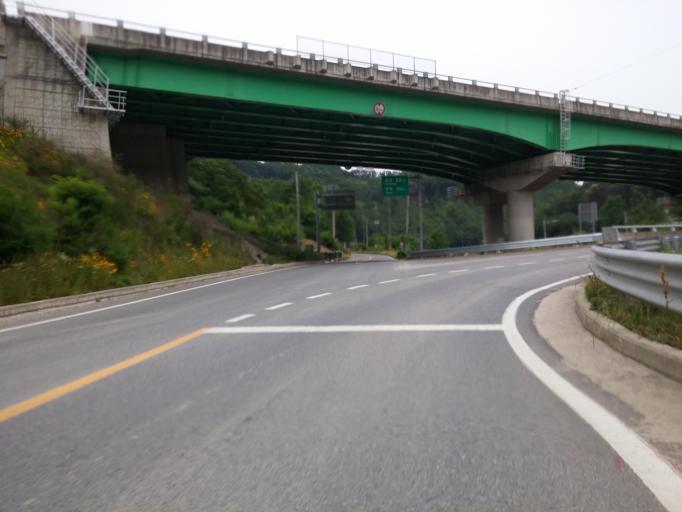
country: KR
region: Chungcheongbuk-do
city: Okcheon
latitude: 36.2531
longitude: 127.5117
